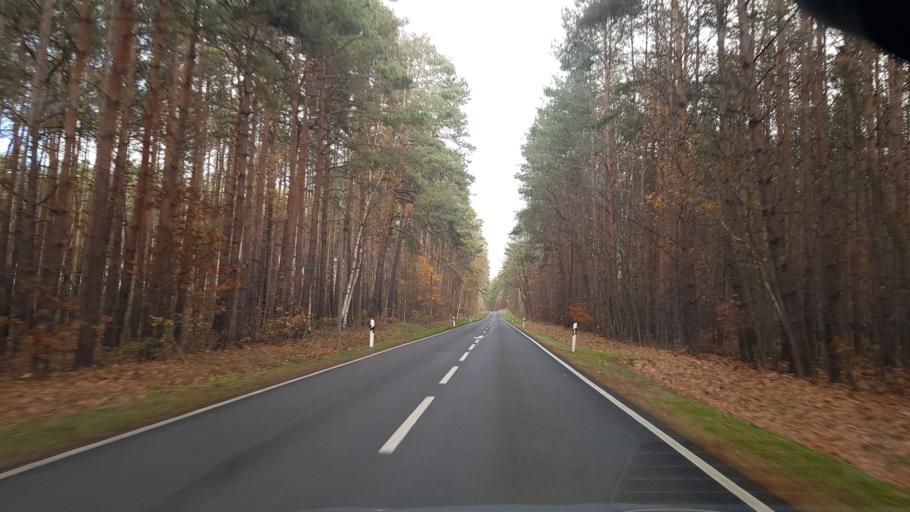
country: DE
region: Brandenburg
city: Sonnewalde
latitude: 51.7208
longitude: 13.6865
